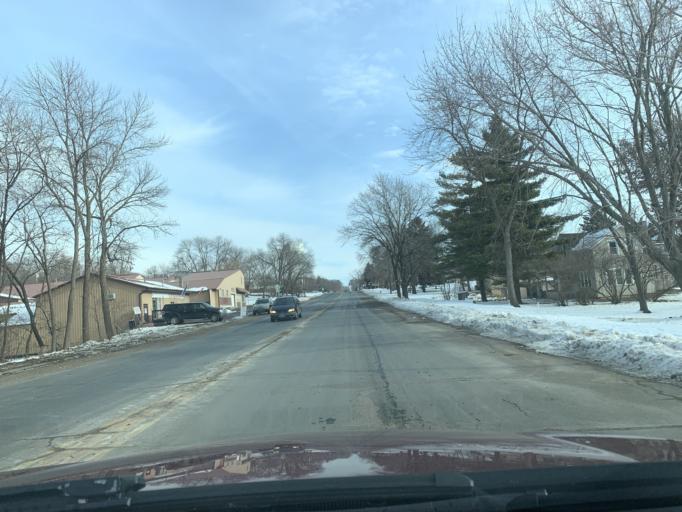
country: US
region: Minnesota
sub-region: Washington County
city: Saint Paul Park
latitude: 44.8478
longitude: -92.9943
